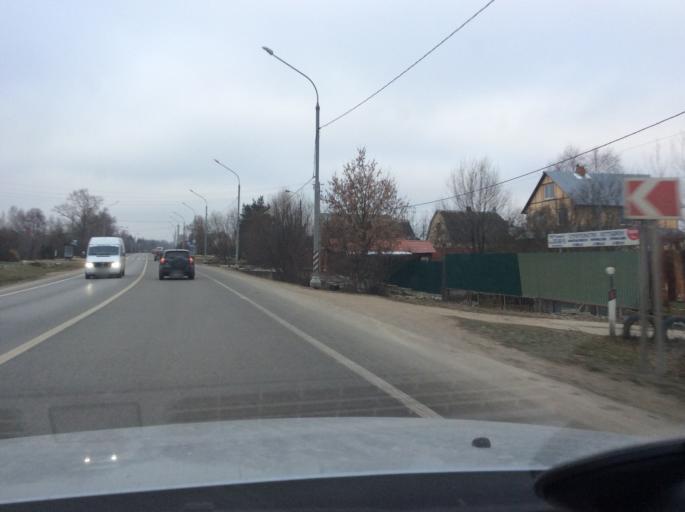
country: RU
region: Moskovskaya
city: Troitsk
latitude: 55.3710
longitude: 37.2021
